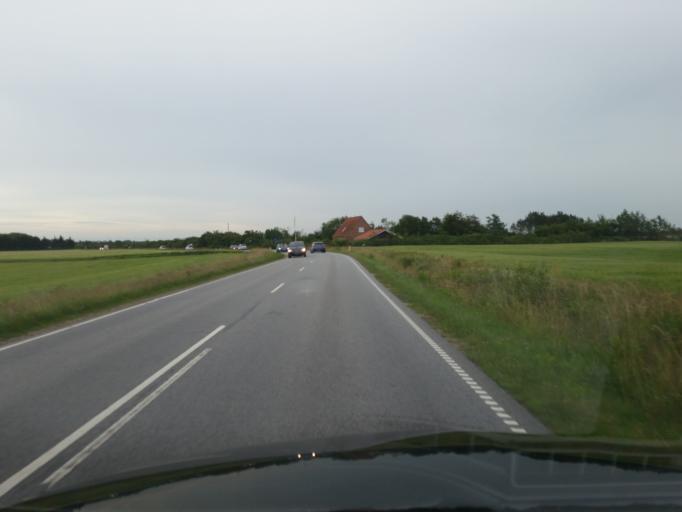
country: DK
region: South Denmark
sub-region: Varde Kommune
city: Oksbol
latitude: 55.7847
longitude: 8.2638
